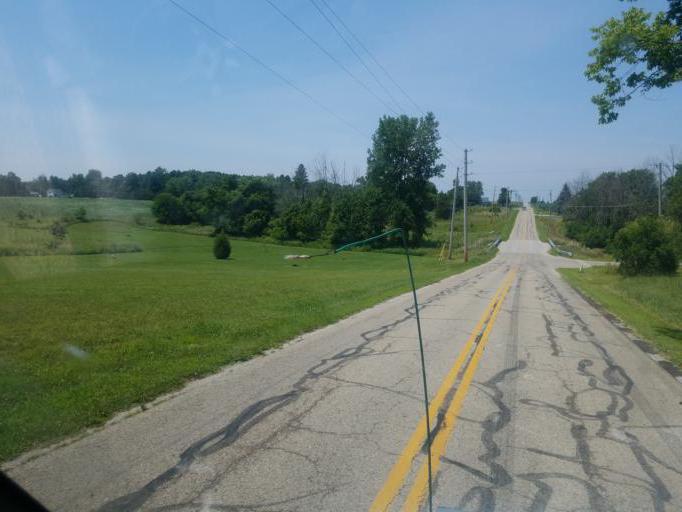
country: US
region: Ohio
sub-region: Logan County
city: De Graff
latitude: 40.3016
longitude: -84.0283
